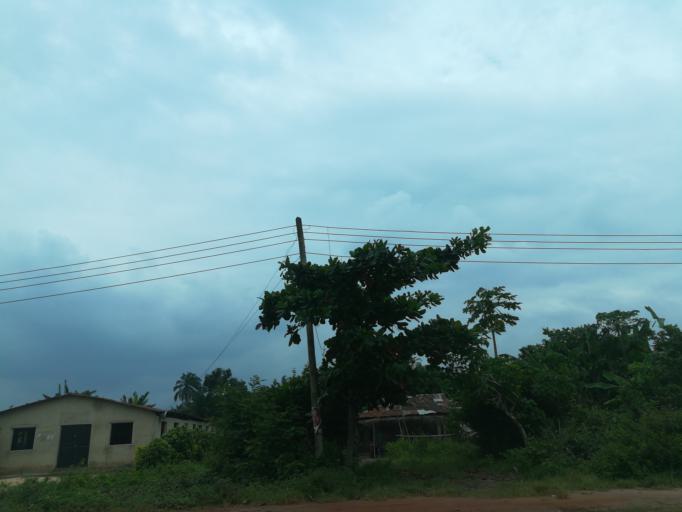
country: NG
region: Lagos
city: Ejirin
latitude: 6.6466
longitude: 3.7784
